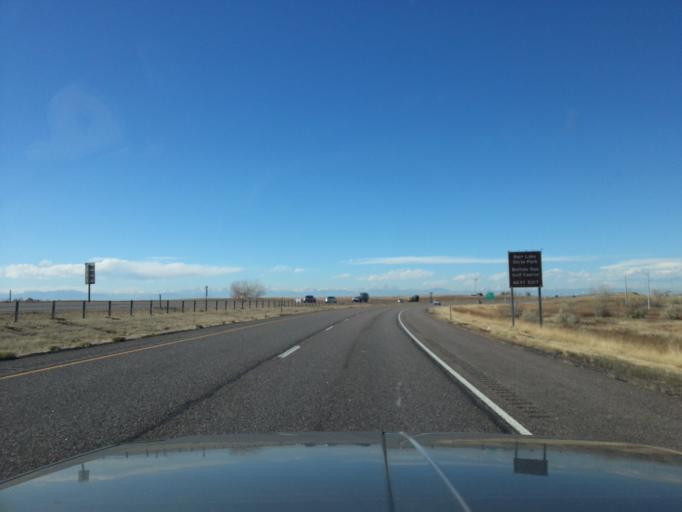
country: US
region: Colorado
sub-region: Adams County
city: Brighton
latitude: 39.9070
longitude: -104.7742
